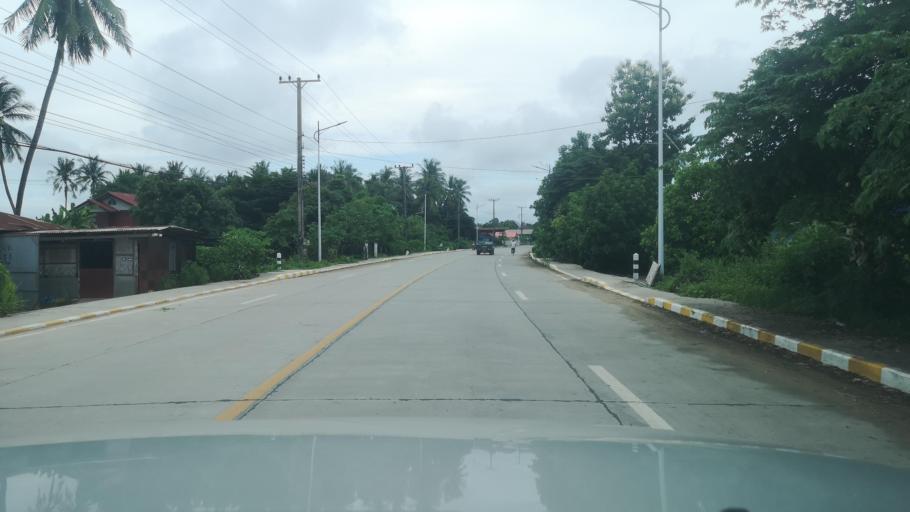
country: TH
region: Nong Khai
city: Tha Bo
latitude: 17.8257
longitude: 102.6576
